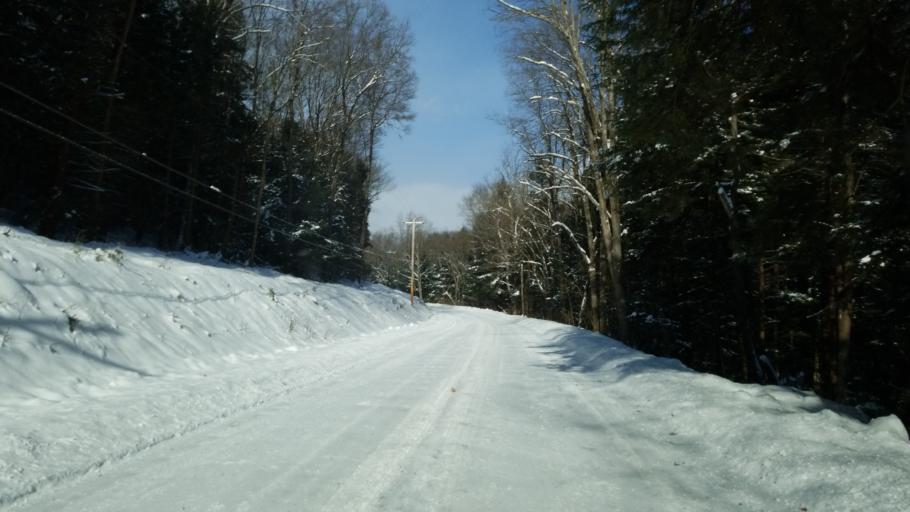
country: US
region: Pennsylvania
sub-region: Clearfield County
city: Clearfield
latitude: 41.0498
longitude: -78.4647
